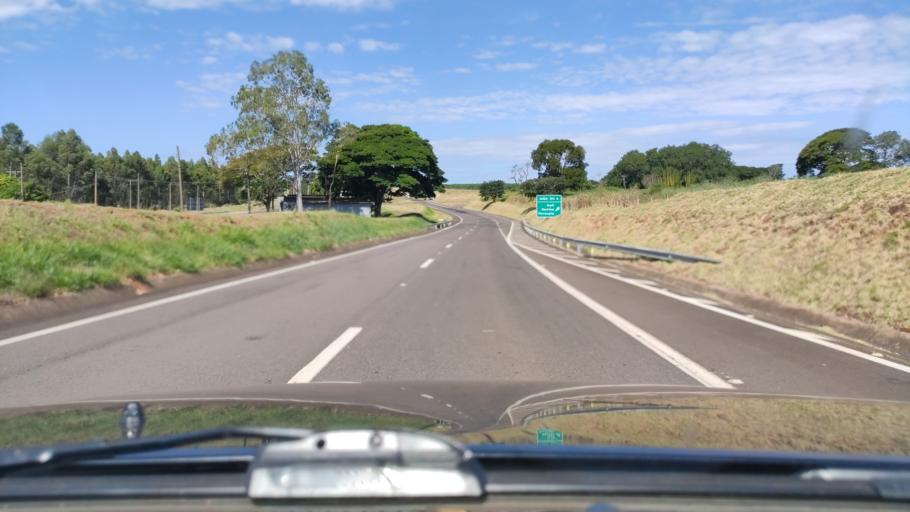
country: BR
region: Sao Paulo
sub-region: Rancharia
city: Rancharia
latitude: -22.4394
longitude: -51.0018
